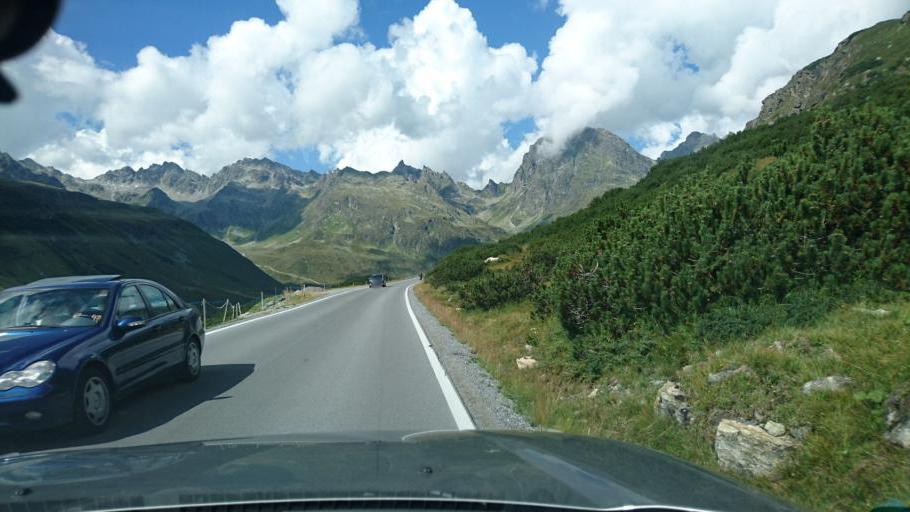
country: AT
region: Vorarlberg
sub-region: Politischer Bezirk Bludenz
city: Gaschurn
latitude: 46.9196
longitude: 10.0764
